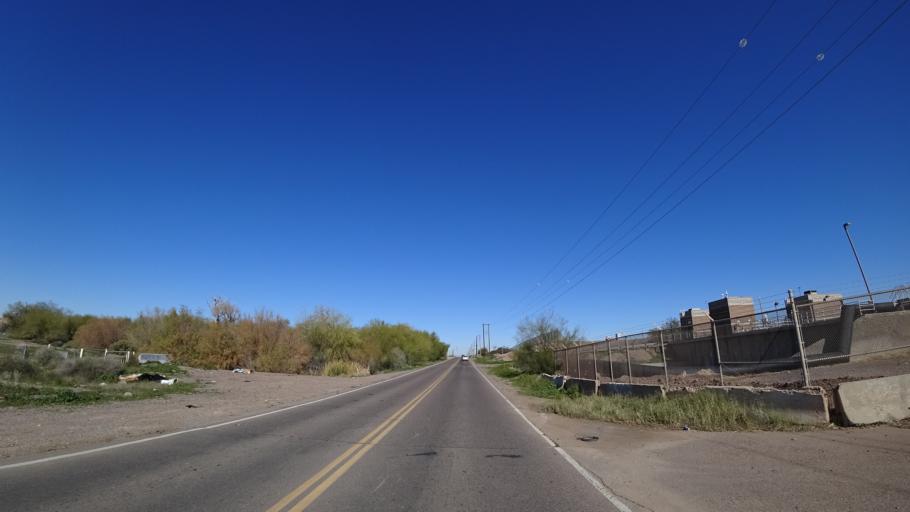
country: US
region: Arizona
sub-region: Maricopa County
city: Tolleson
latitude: 33.3886
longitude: -112.2543
